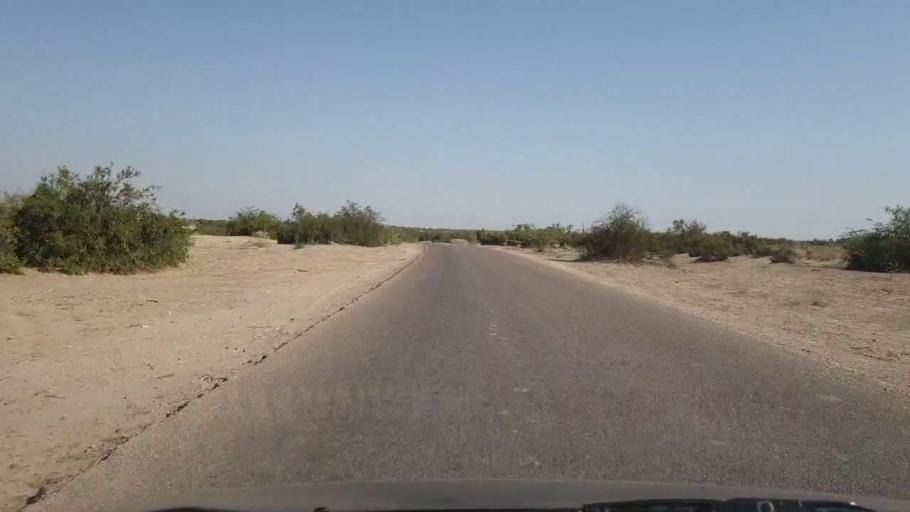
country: PK
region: Sindh
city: Chor
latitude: 25.5032
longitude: 69.8158
